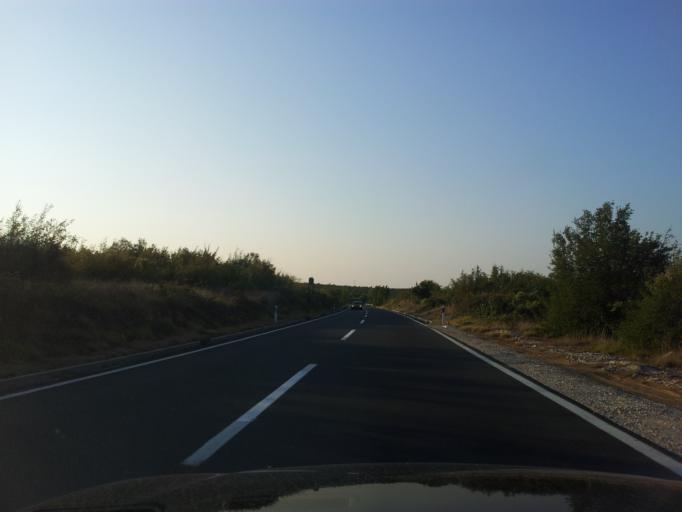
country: HR
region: Zadarska
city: Benkovac
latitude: 44.0131
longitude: 15.5709
